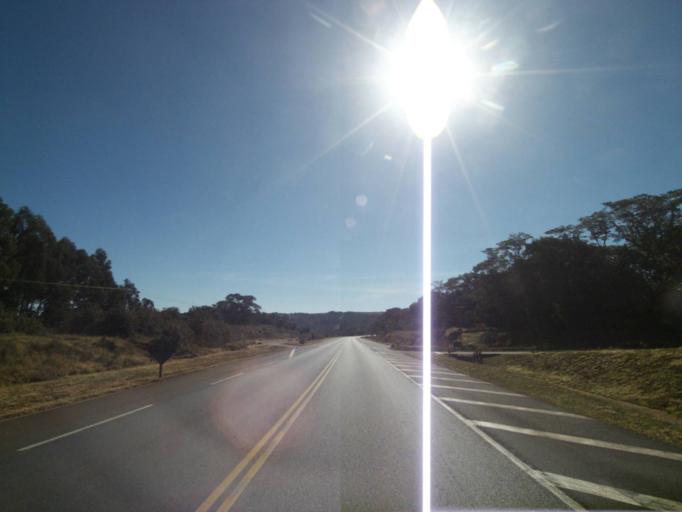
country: BR
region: Parana
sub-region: Tibagi
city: Tibagi
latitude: -24.4056
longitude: -50.3434
